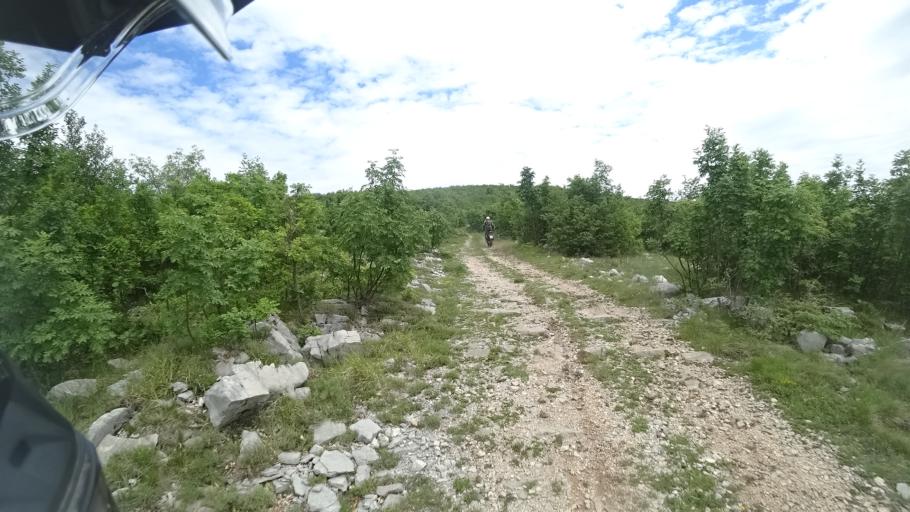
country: HR
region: Splitsko-Dalmatinska
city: Hrvace
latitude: 43.8840
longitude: 16.5876
